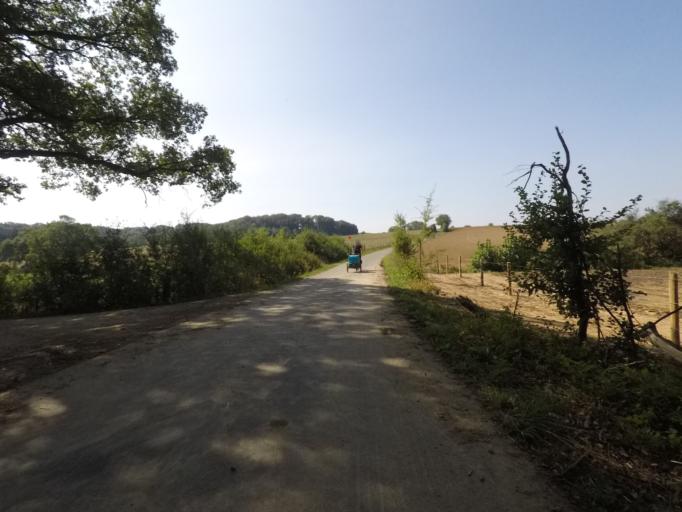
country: LU
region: Luxembourg
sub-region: Canton de Capellen
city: Mamer
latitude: 49.6497
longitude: 6.0221
